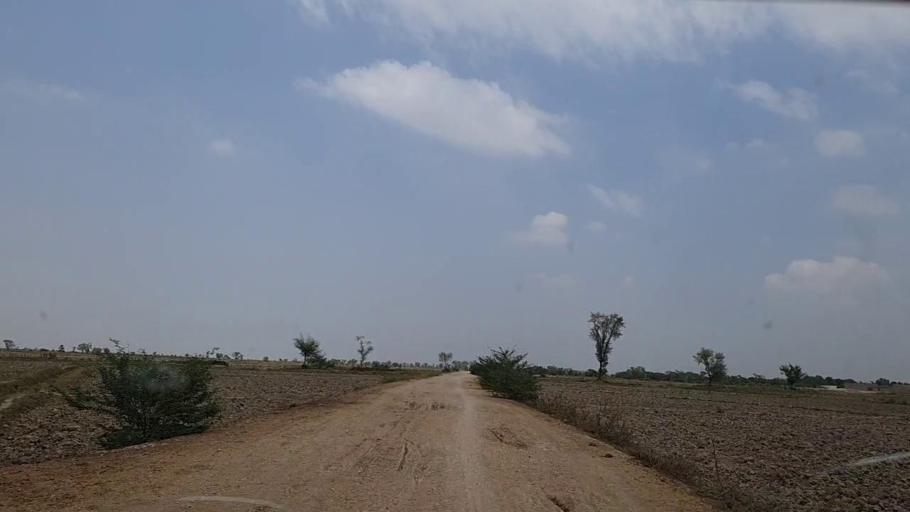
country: PK
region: Sindh
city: Phulji
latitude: 26.8248
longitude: 67.6405
